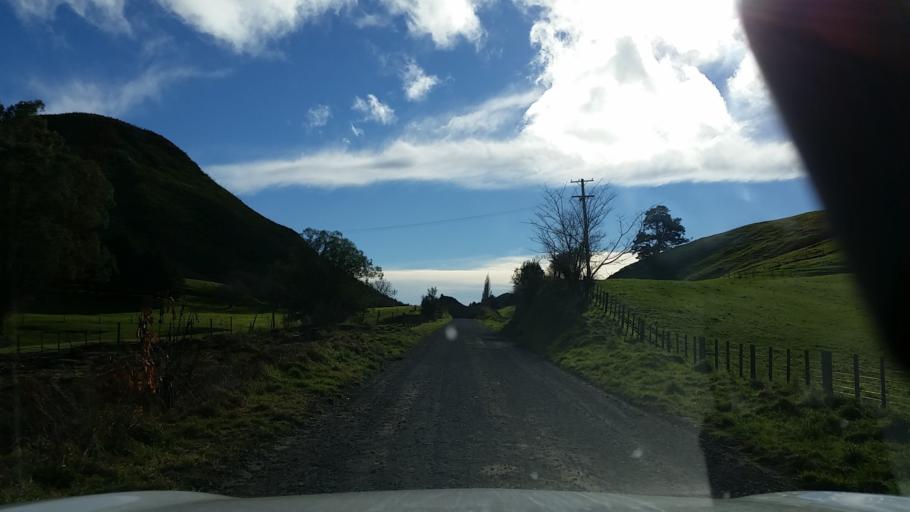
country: NZ
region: Bay of Plenty
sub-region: Rotorua District
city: Rotorua
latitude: -38.3665
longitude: 176.2076
